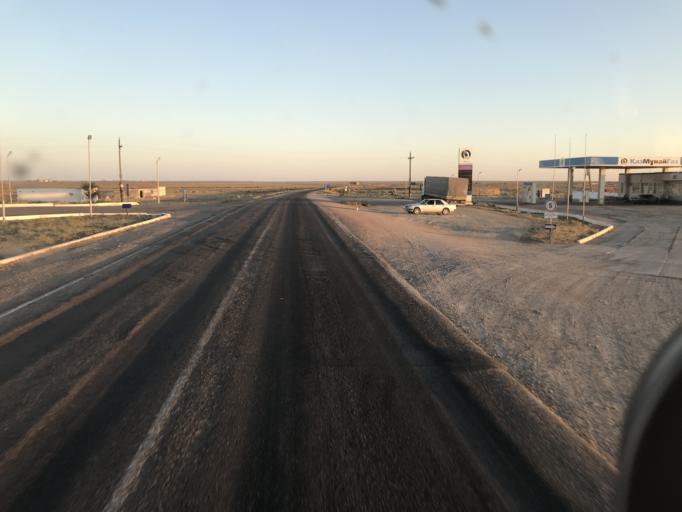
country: KZ
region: Qaraghandy
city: Saryshaghan
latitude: 46.0201
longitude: 73.5916
